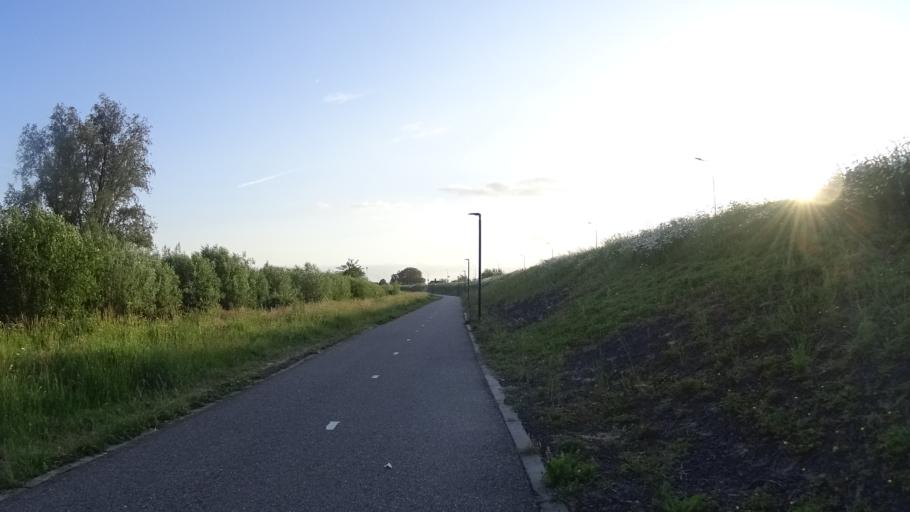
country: NL
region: North Brabant
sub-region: Gemeente Werkendam
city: Werkendam
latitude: 51.8300
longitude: 4.9072
